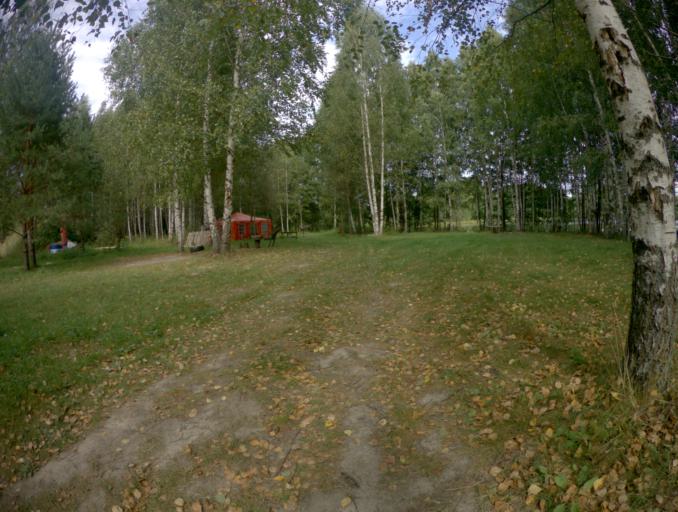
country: RU
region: Vladimir
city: Golovino
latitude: 55.9103
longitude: 40.5573
